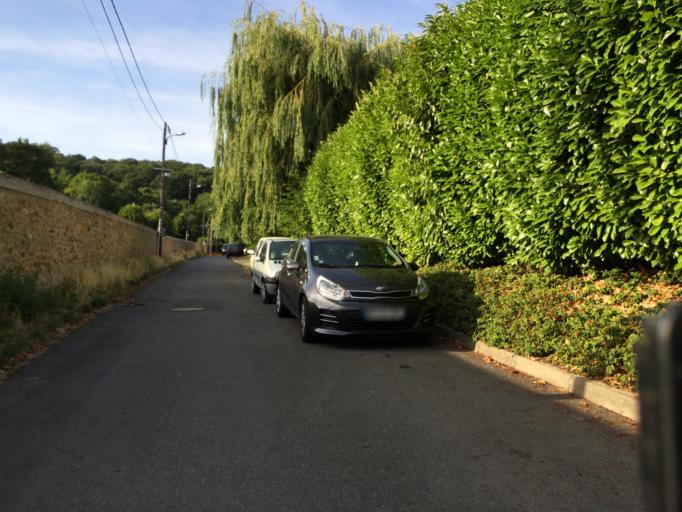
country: FR
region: Ile-de-France
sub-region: Departement de l'Essonne
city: Igny
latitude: 48.7398
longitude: 2.2446
